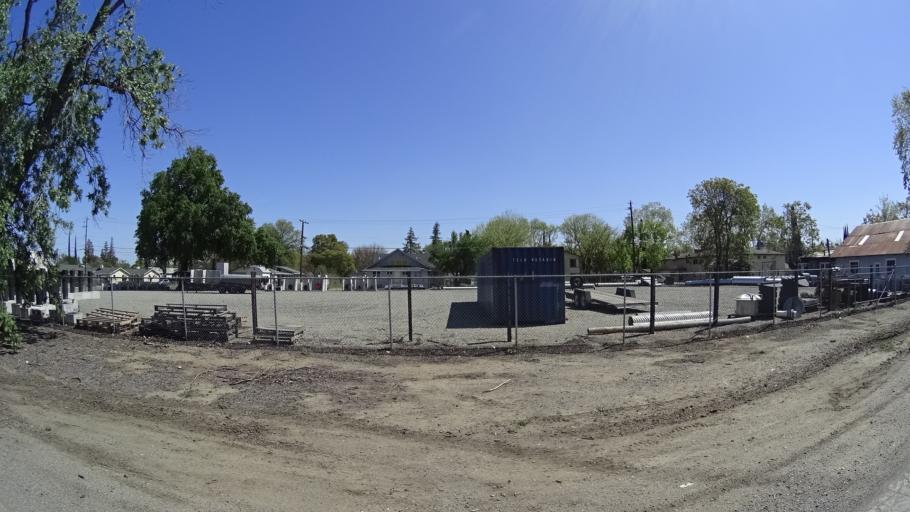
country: US
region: California
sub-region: Glenn County
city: Willows
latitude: 39.5214
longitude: -122.1923
